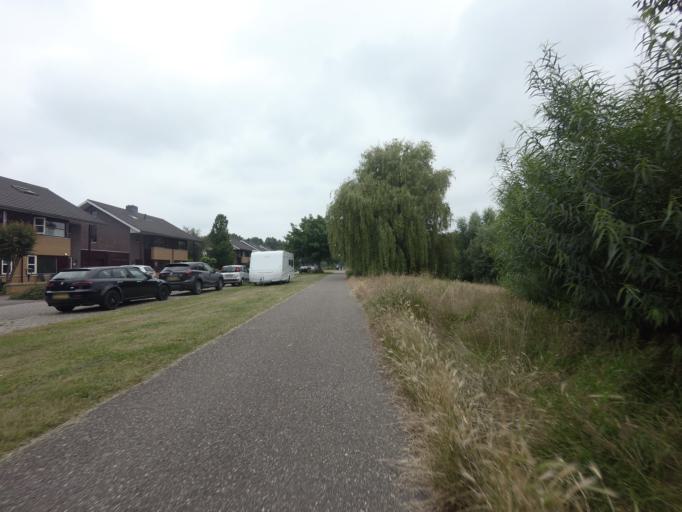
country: NL
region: Flevoland
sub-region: Gemeente Almere
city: Almere Stad
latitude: 52.4032
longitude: 5.2820
